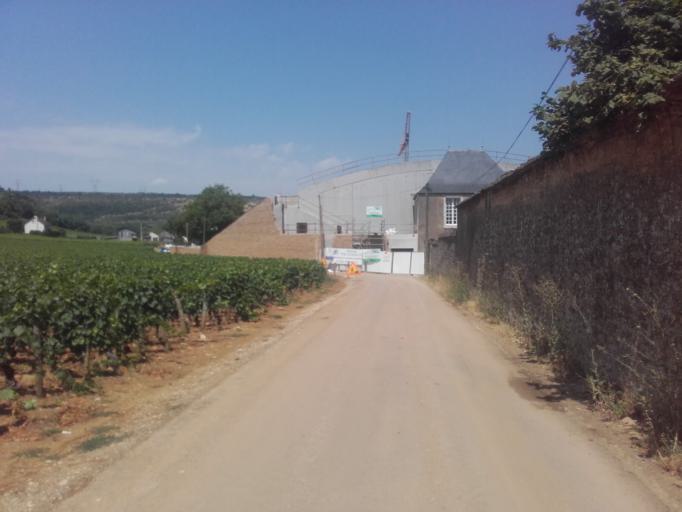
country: FR
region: Bourgogne
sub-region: Departement de la Cote-d'Or
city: Nuits-Saint-Georges
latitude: 47.1363
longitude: 4.9447
